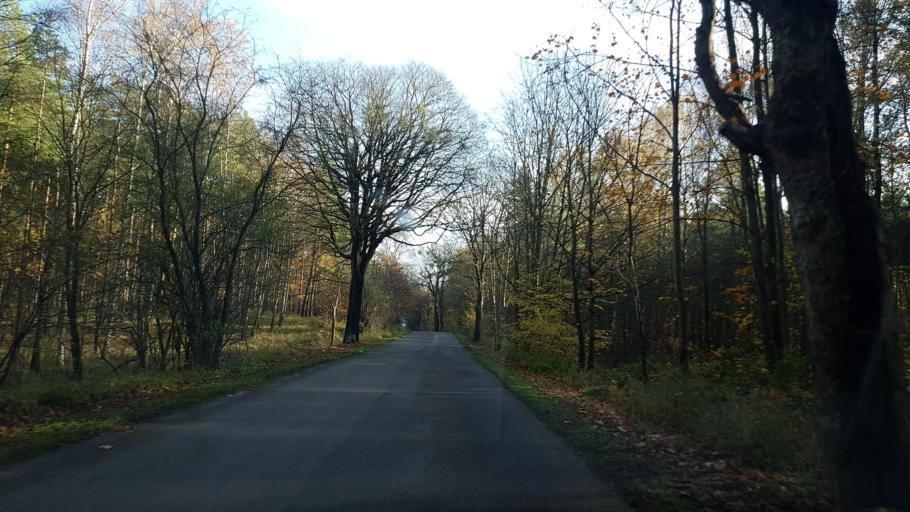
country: PL
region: West Pomeranian Voivodeship
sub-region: Powiat policki
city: Dobra
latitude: 53.5005
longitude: 14.3432
